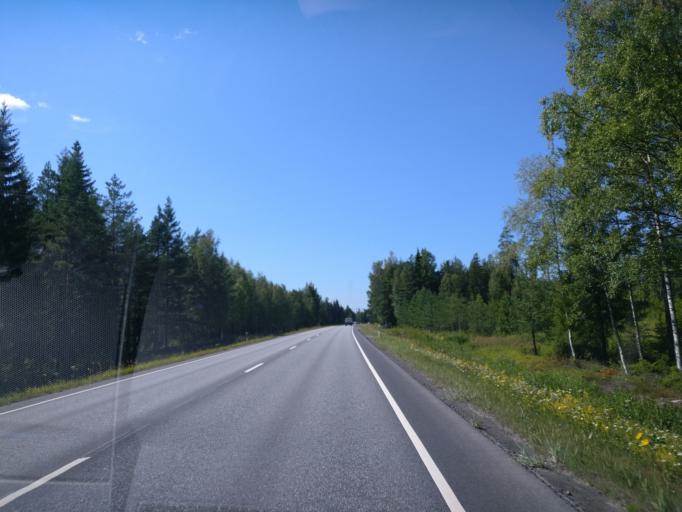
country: FI
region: Satakunta
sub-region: Pori
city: Kullaa
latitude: 61.4574
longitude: 22.0608
